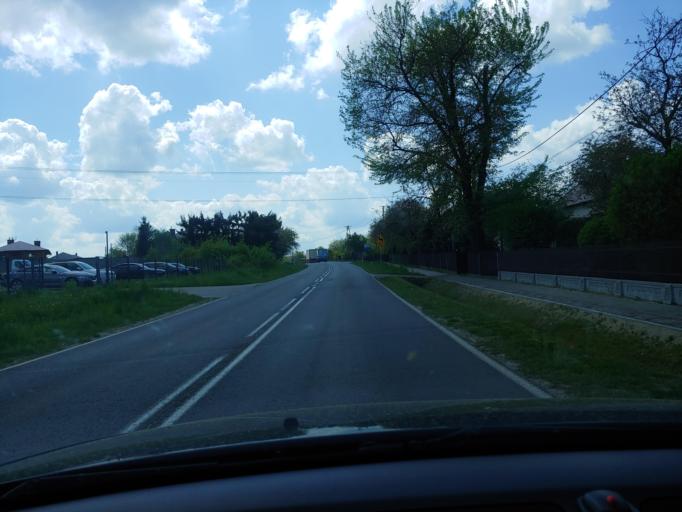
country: PL
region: Subcarpathian Voivodeship
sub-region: Powiat mielecki
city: Radomysl Wielki
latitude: 50.1914
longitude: 21.2693
